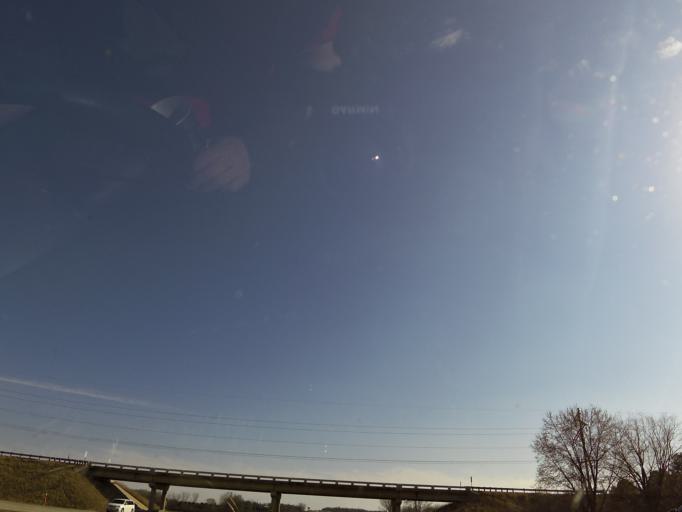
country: US
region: Minnesota
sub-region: Steele County
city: Owatonna
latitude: 44.0526
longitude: -93.2499
